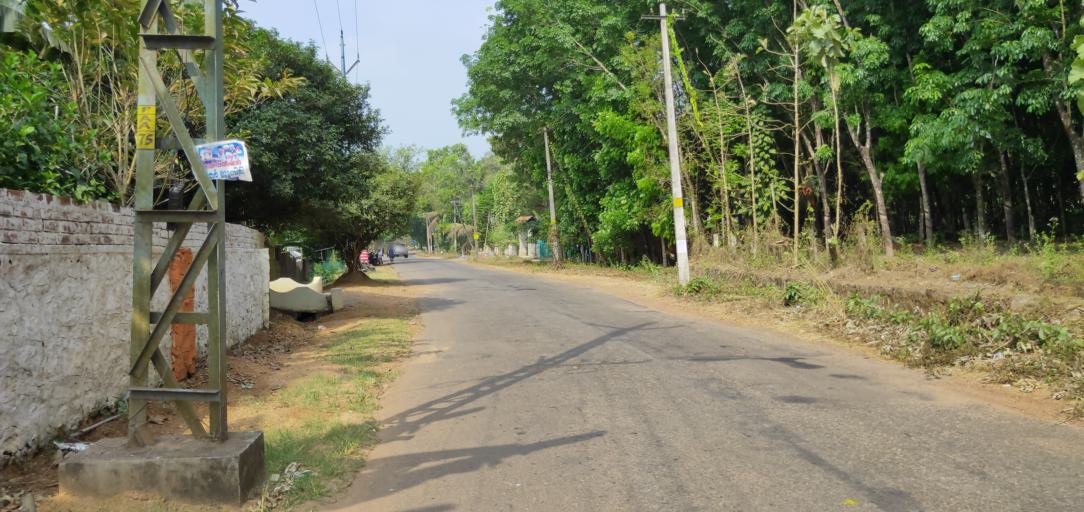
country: IN
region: Kerala
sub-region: Malappuram
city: Manjeri
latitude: 11.2305
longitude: 76.2772
